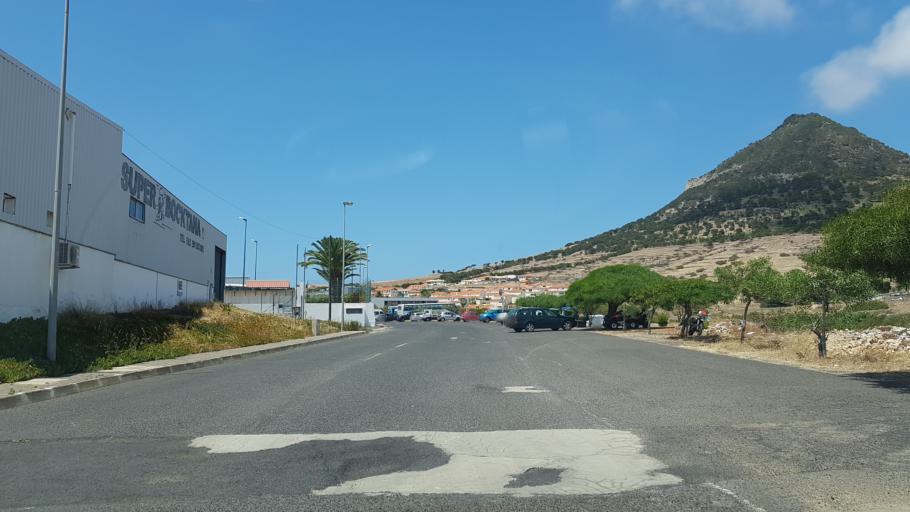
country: PT
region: Madeira
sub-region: Porto Santo
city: Vila de Porto Santo
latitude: 33.0692
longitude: -16.3424
